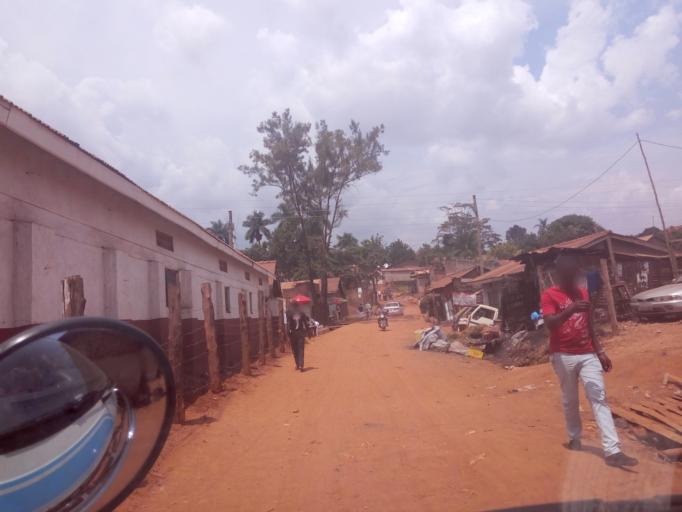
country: UG
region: Central Region
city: Kampala Central Division
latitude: 0.3483
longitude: 32.5607
